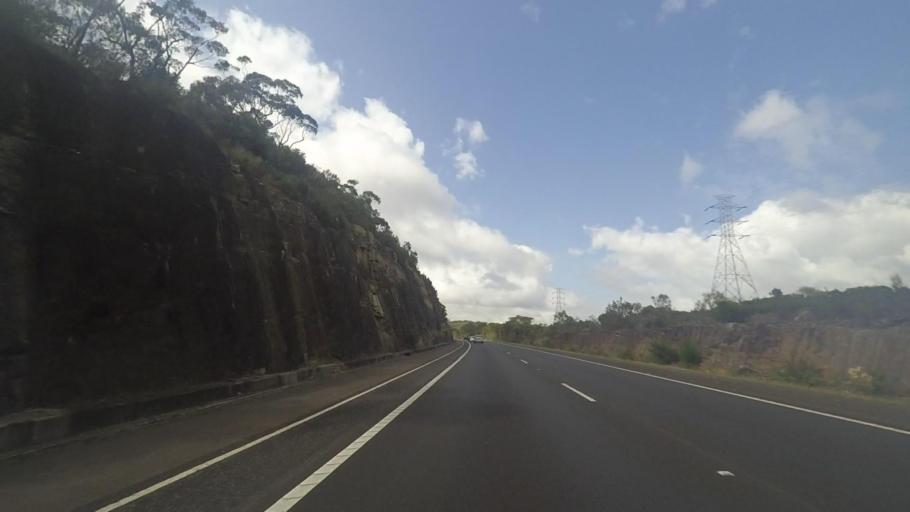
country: AU
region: New South Wales
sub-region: Wollongong
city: Helensburgh
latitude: -34.1913
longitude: 150.9672
